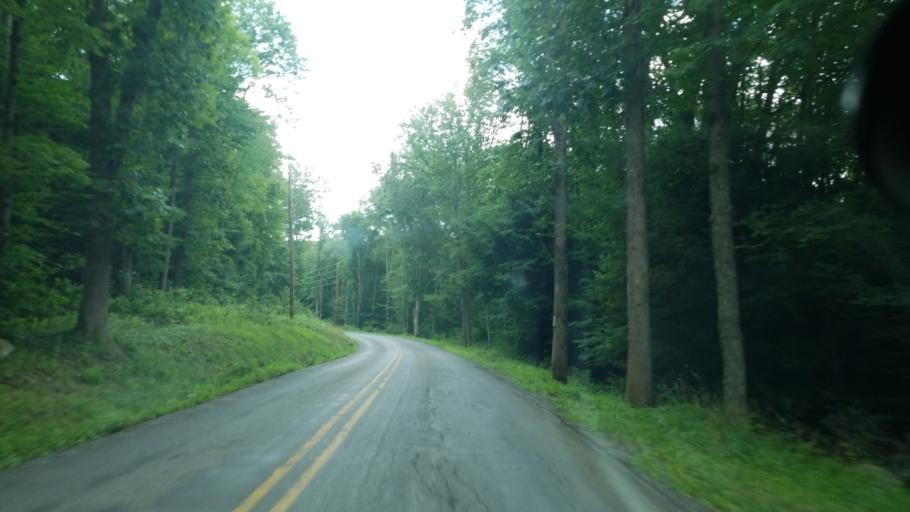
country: US
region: Pennsylvania
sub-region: Jefferson County
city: Brookville
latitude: 41.2282
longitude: -79.0566
